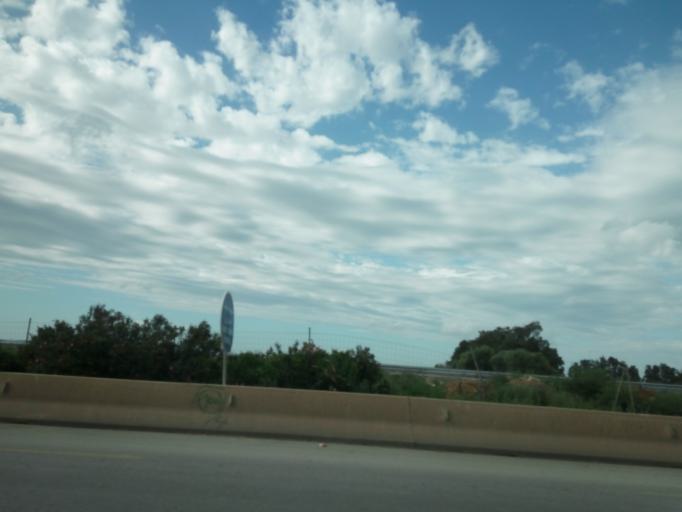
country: DZ
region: Tipaza
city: Mouzaia
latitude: 36.4497
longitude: 2.6830
